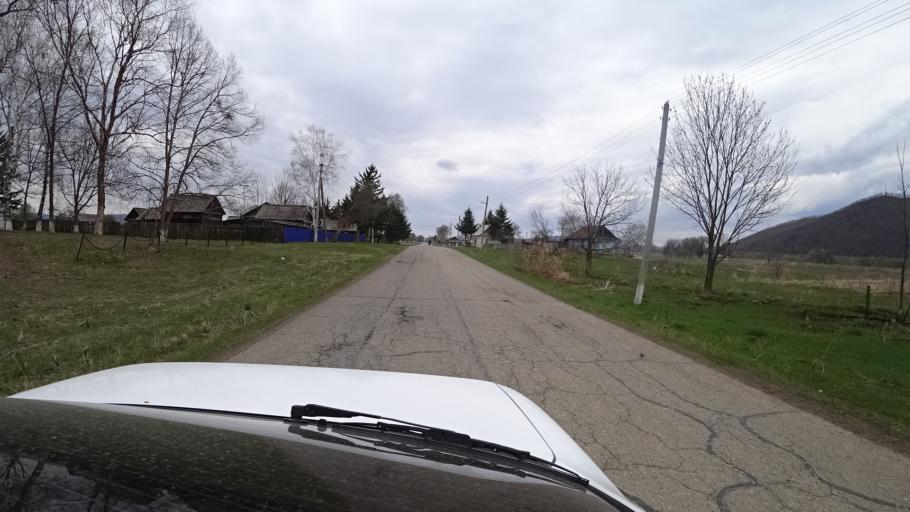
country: RU
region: Primorskiy
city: Novopokrovka
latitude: 45.5754
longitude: 134.3159
